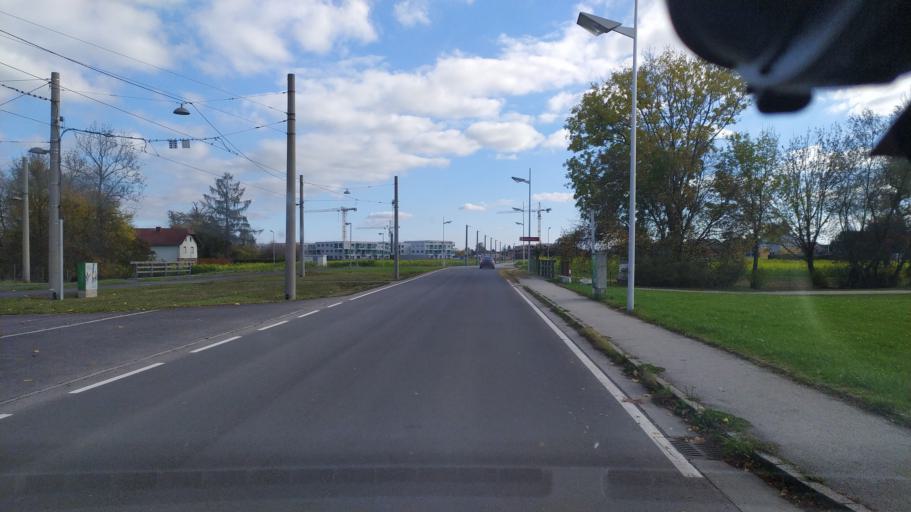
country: AT
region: Upper Austria
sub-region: Politischer Bezirk Urfahr-Umgebung
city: Steyregg
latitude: 48.2567
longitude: 14.3631
